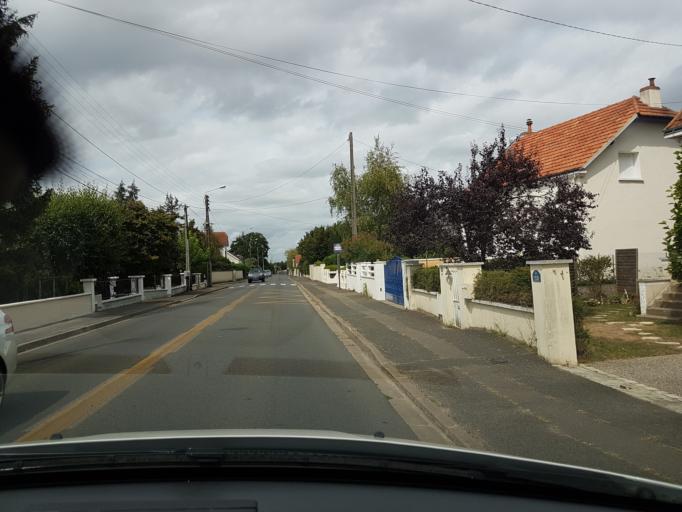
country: FR
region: Centre
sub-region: Departement d'Indre-et-Loire
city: Saint-Avertin
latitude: 47.3494
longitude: 0.7340
